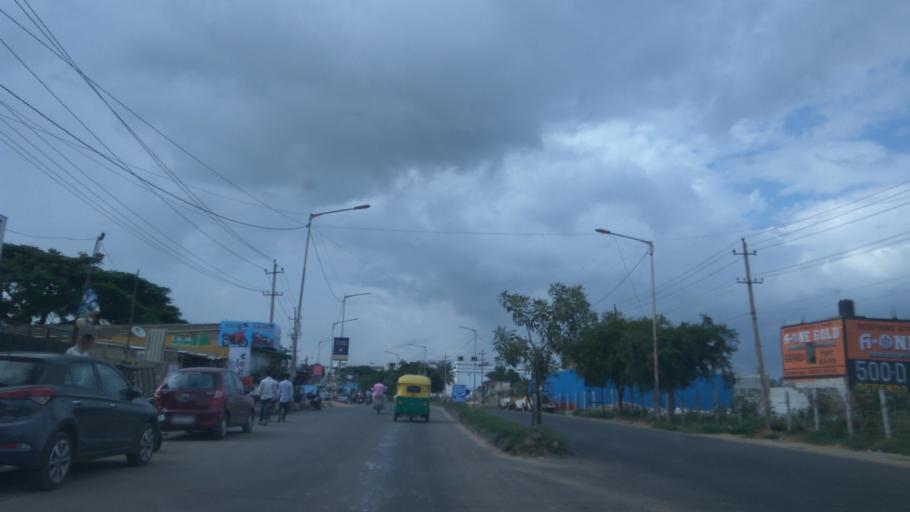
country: IN
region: Karnataka
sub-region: Bangalore Urban
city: Yelahanka
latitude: 13.0623
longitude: 77.6334
